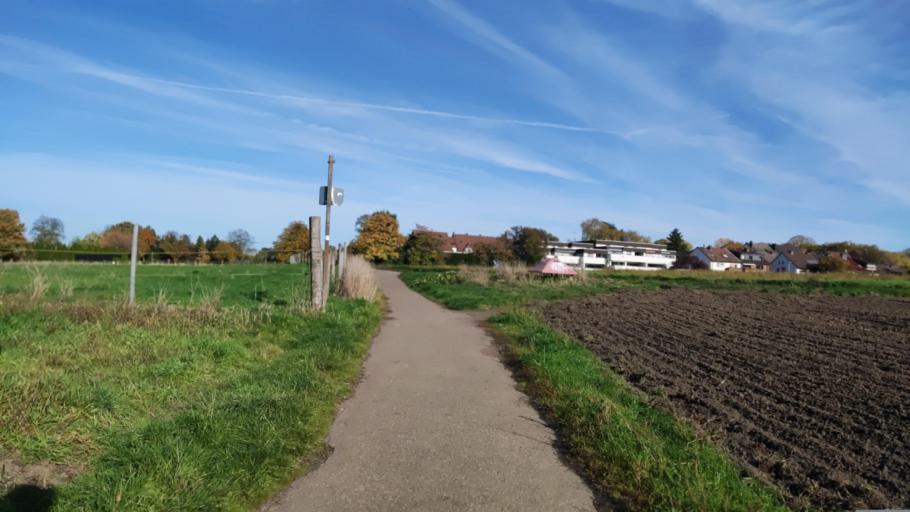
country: DE
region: North Rhine-Westphalia
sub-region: Regierungsbezirk Arnsberg
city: Herne
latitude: 51.5303
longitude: 7.2347
